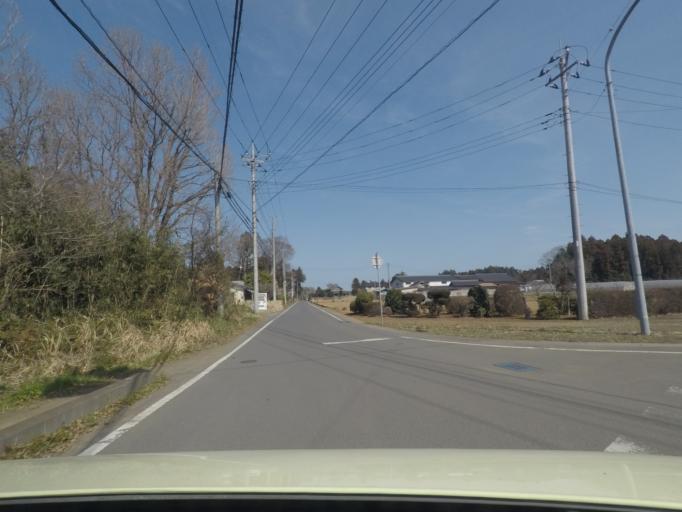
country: JP
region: Ibaraki
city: Okunoya
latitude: 36.2026
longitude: 140.4159
